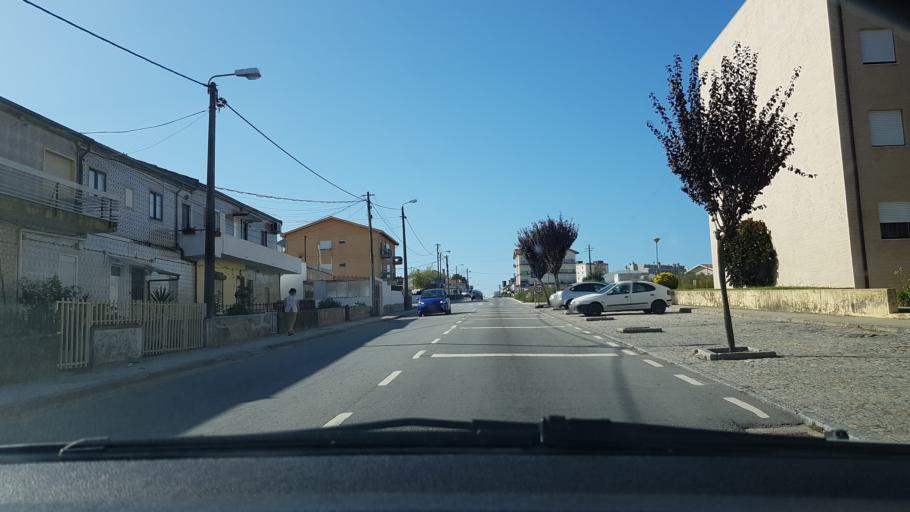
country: PT
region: Porto
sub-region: Gondomar
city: Baguim do Monte
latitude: 41.1830
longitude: -8.5376
